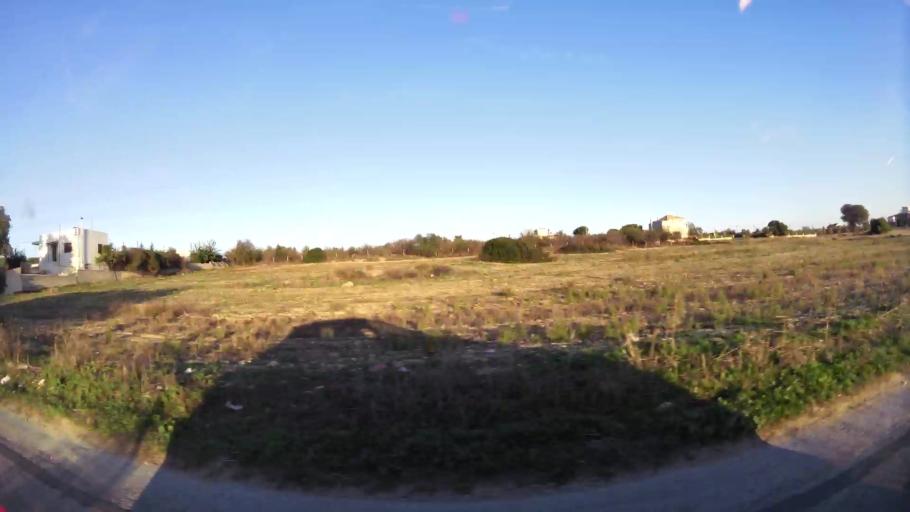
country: GR
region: Attica
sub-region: Nomarchia Anatolikis Attikis
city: Rafina
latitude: 38.0018
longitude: 24.0095
